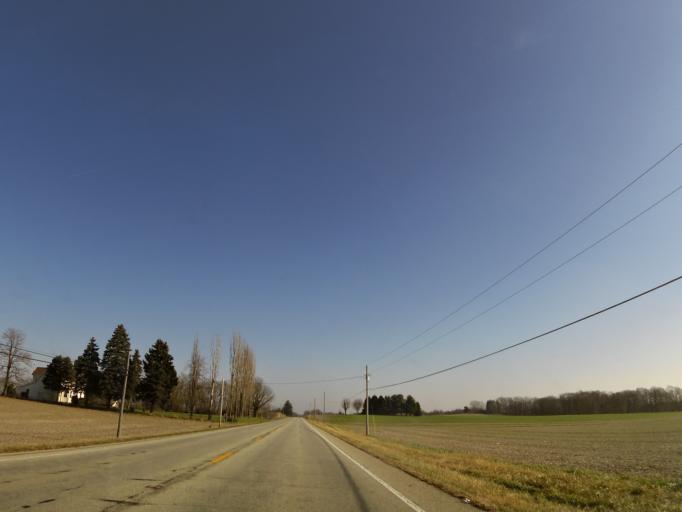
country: US
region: Indiana
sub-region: Fayette County
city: Connersville
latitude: 39.6309
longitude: -85.2351
